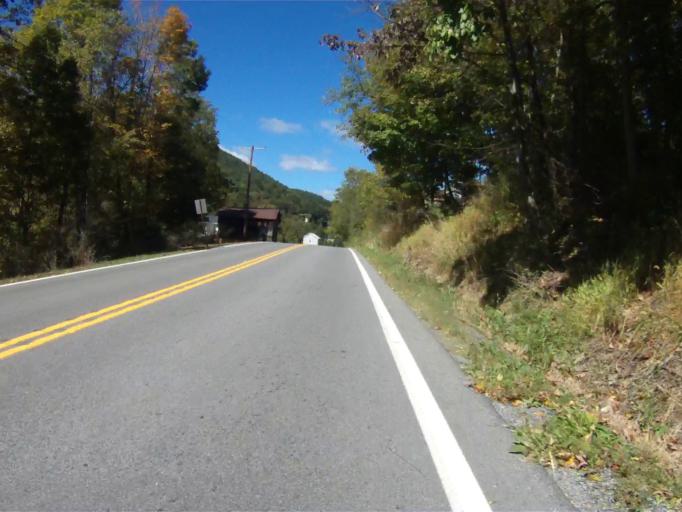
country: US
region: Pennsylvania
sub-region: Centre County
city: Milesburg
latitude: 40.9131
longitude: -77.8868
